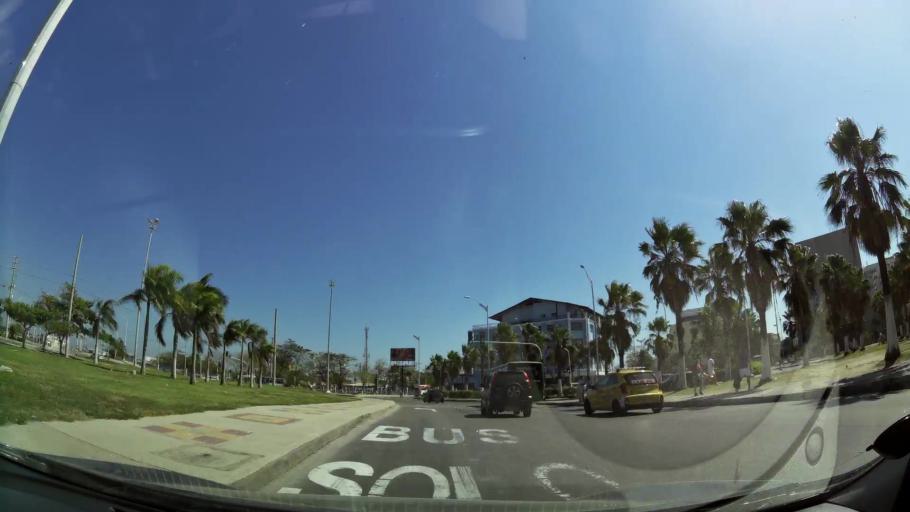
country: CO
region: Atlantico
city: Barranquilla
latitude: 10.9855
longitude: -74.7768
